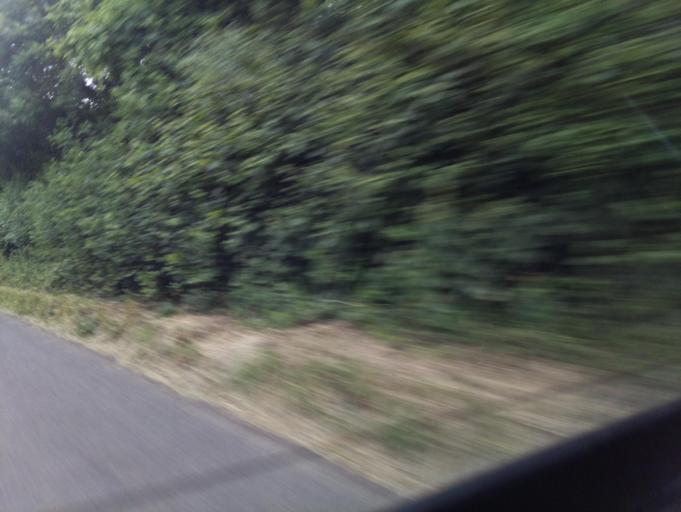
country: GB
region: England
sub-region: Somerset
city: Yeovil
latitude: 50.9206
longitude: -2.5862
